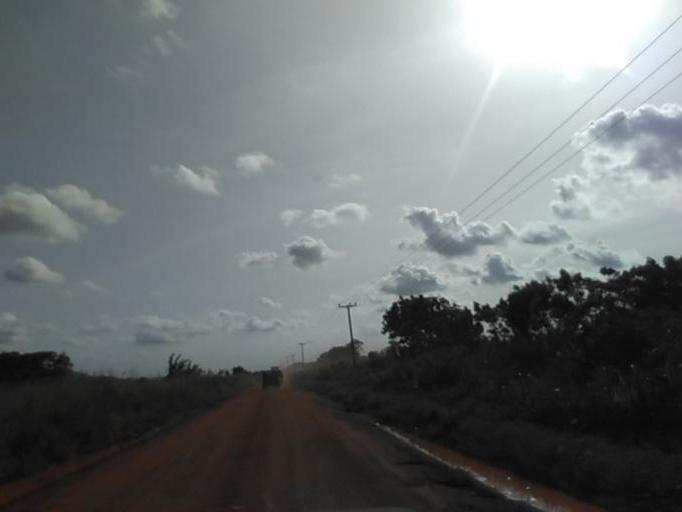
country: GH
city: Akropong
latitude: 6.0963
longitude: 0.2446
